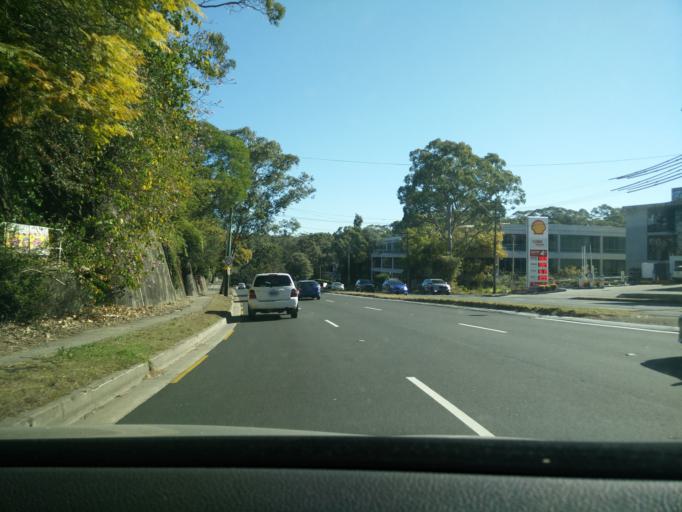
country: AU
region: New South Wales
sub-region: City of Sydney
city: Pymble
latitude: -33.7521
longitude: 151.1443
